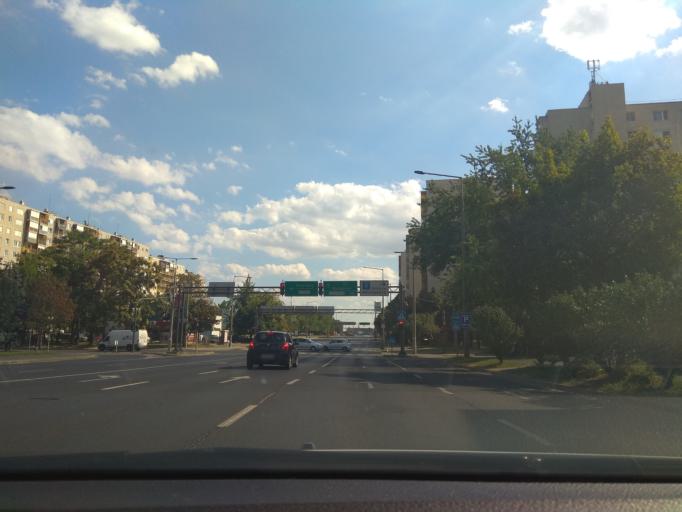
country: HU
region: Borsod-Abauj-Zemplen
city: Miskolc
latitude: 48.1007
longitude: 20.7921
